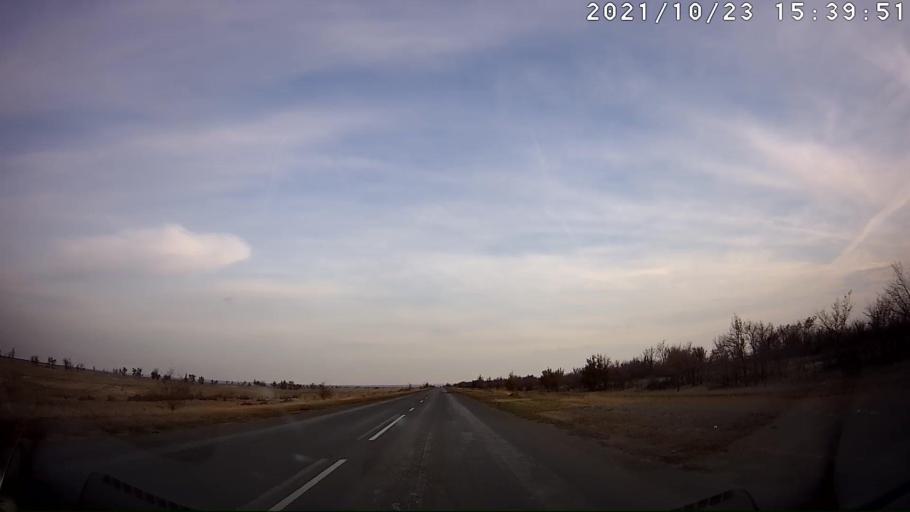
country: RU
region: Volgograd
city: Bereslavka
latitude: 48.1194
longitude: 44.1330
